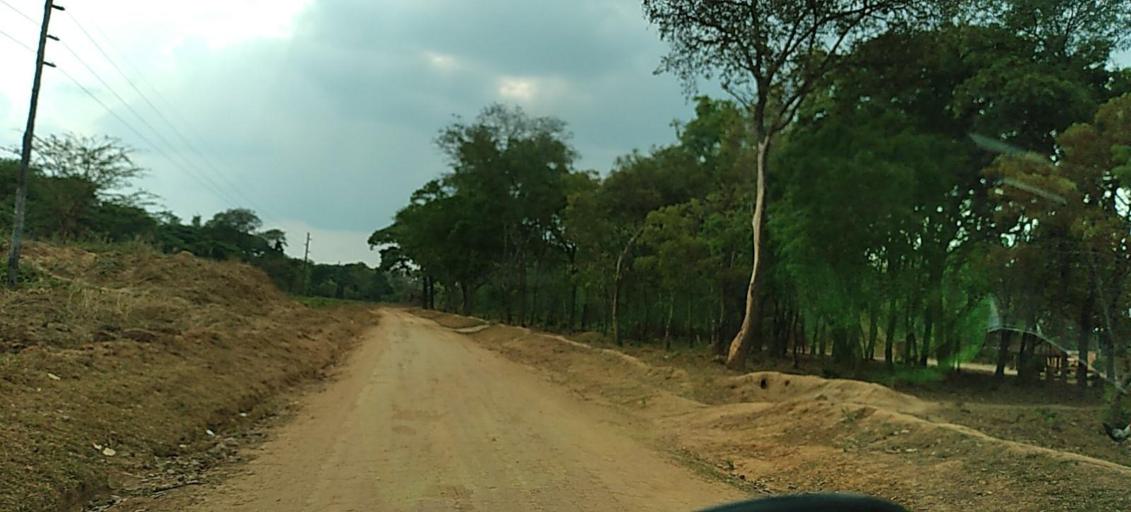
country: ZM
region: North-Western
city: Solwezi
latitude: -12.7847
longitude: 26.5068
